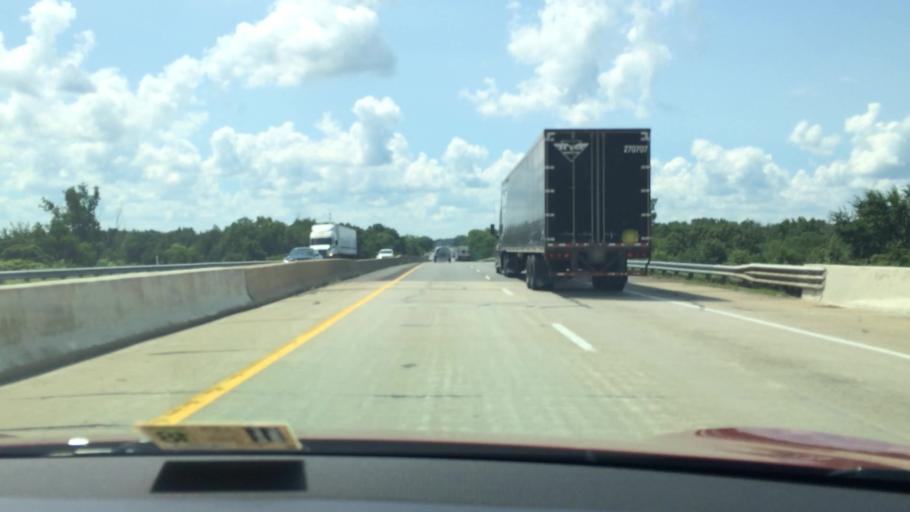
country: US
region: Indiana
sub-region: Saint Joseph County
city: South Bend
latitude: 41.6873
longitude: -86.3410
